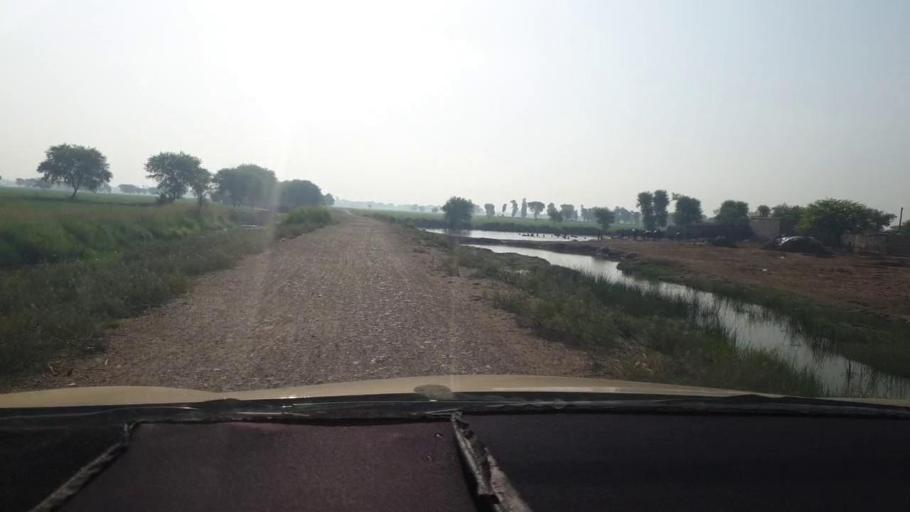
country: PK
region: Sindh
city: Kambar
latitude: 27.5941
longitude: 68.1083
